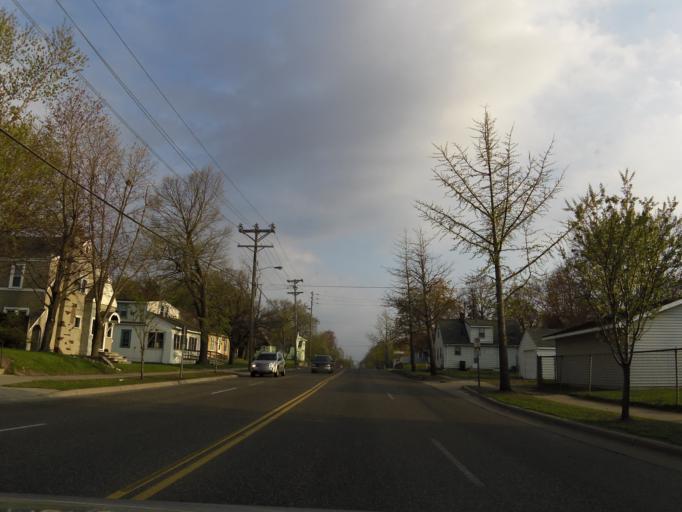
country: US
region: Minnesota
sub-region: Ramsey County
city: Maplewood
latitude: 44.9622
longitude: -93.0254
